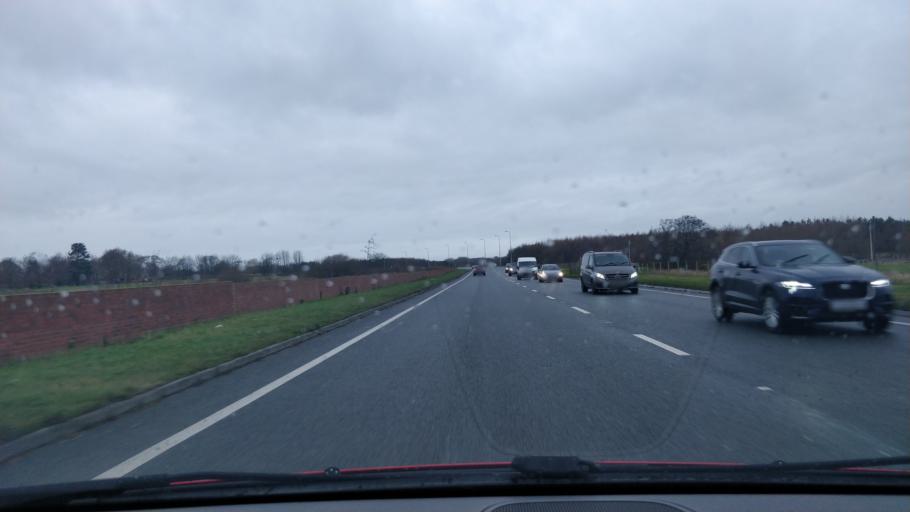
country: GB
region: England
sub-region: Sefton
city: Thornton
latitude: 53.5024
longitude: -2.9905
